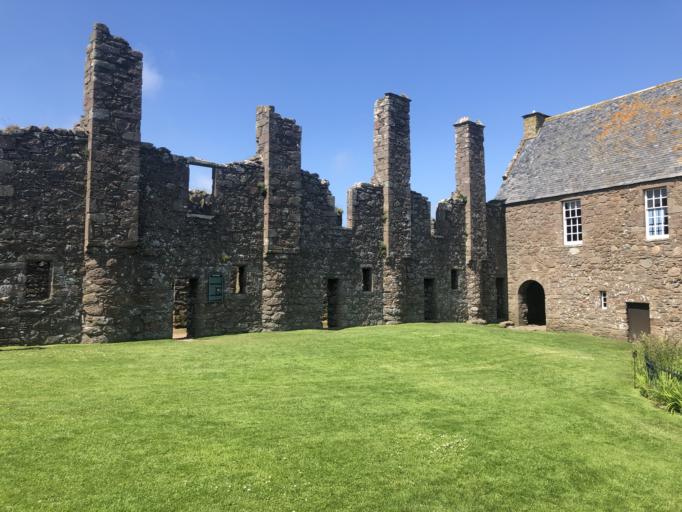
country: GB
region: Scotland
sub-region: Aberdeenshire
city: Stonehaven
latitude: 56.9459
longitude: -2.1964
